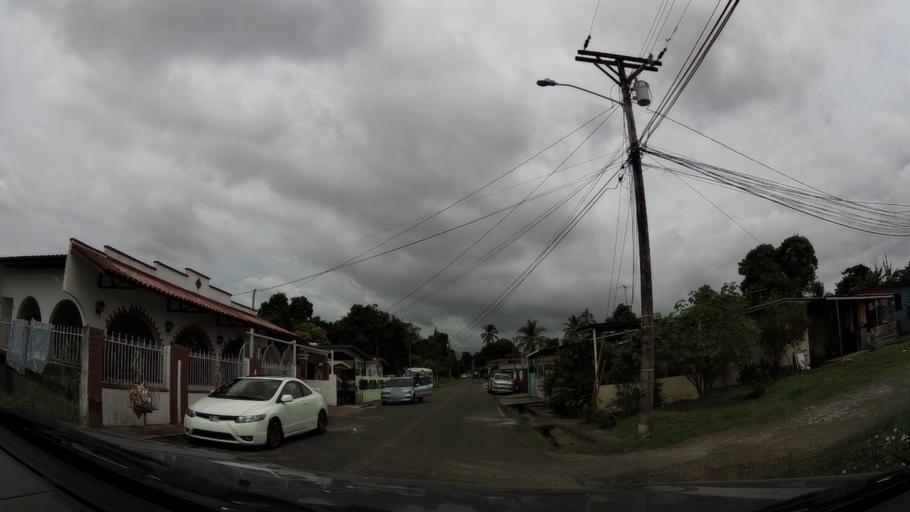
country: PA
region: Panama
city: San Miguelito
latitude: 9.0413
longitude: -79.4325
